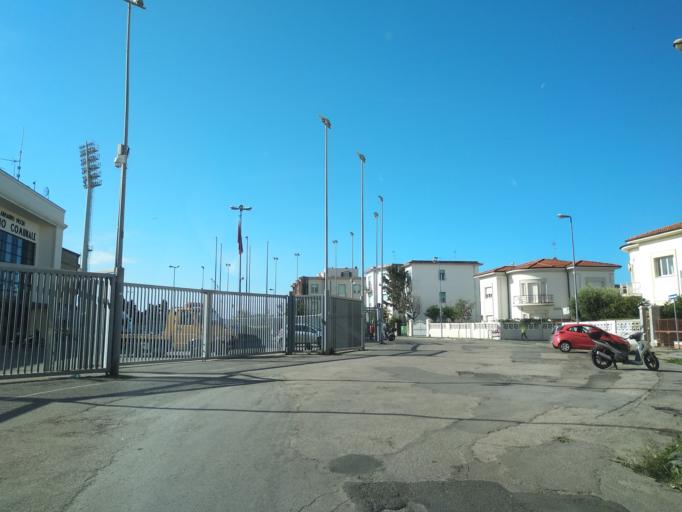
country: IT
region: Tuscany
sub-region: Provincia di Livorno
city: Livorno
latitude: 43.5270
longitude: 10.3132
